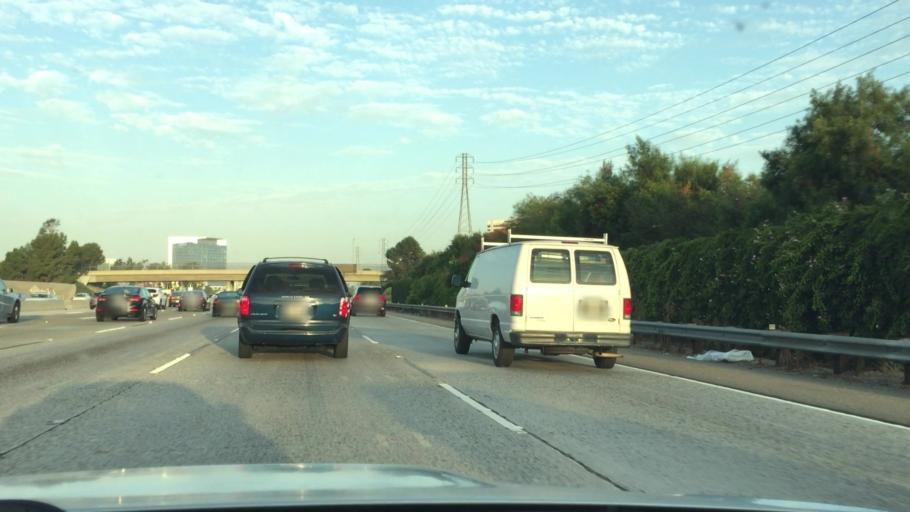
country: US
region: California
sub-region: Orange County
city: Irvine
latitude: 33.6717
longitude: -117.8292
